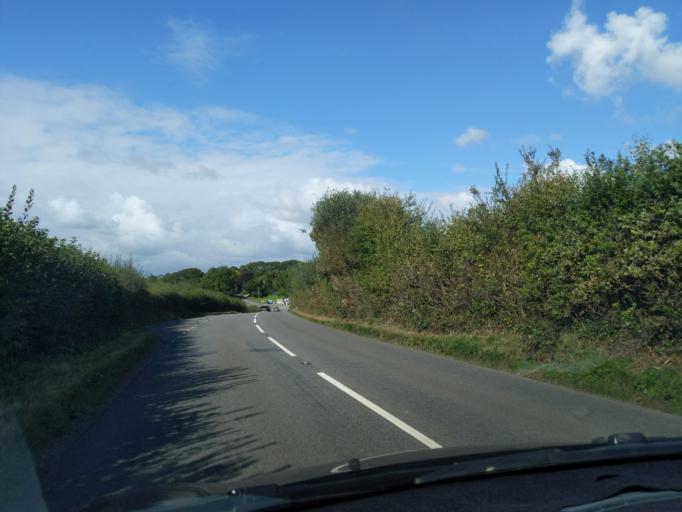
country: GB
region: England
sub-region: Devon
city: Holsworthy
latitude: 50.7912
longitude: -4.3394
